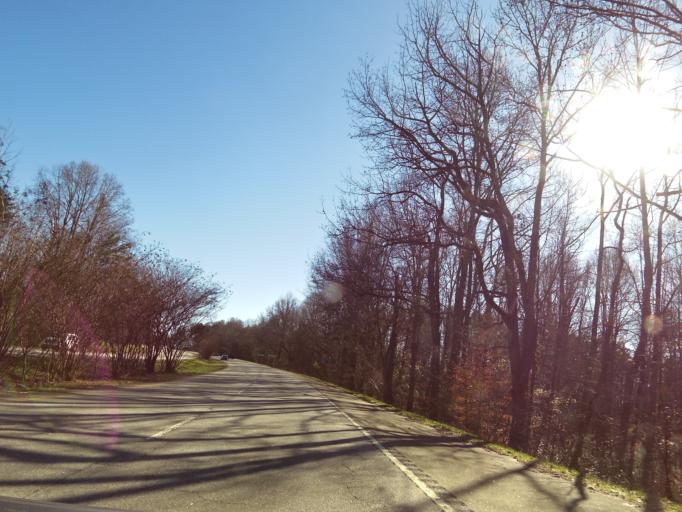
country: US
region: South Carolina
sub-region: Greenville County
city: Berea
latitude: 34.9179
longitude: -82.4327
